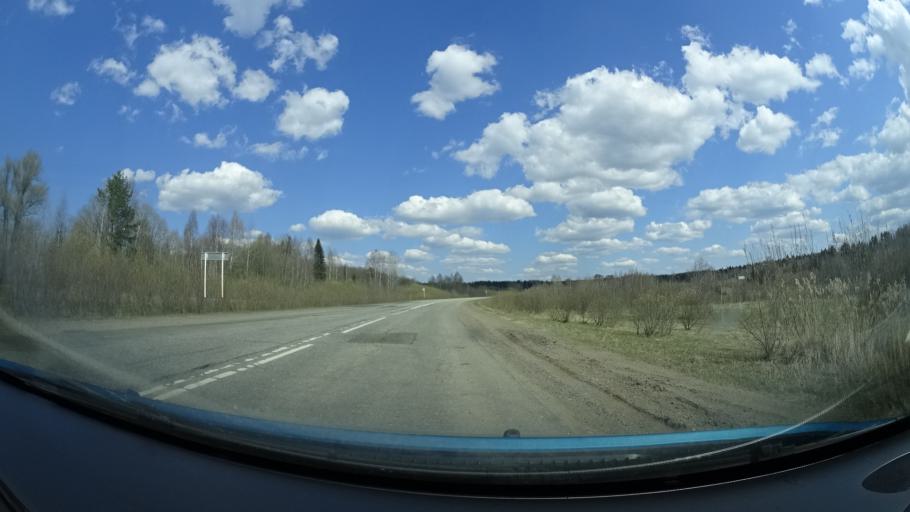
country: RU
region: Perm
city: Osa
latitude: 57.3921
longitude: 55.6103
